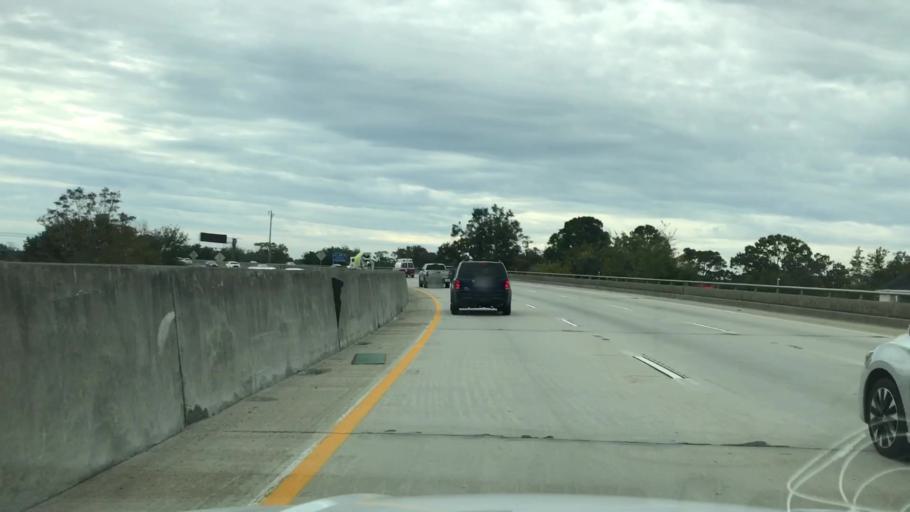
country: US
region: South Carolina
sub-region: Charleston County
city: Charleston
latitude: 32.8140
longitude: -79.9539
